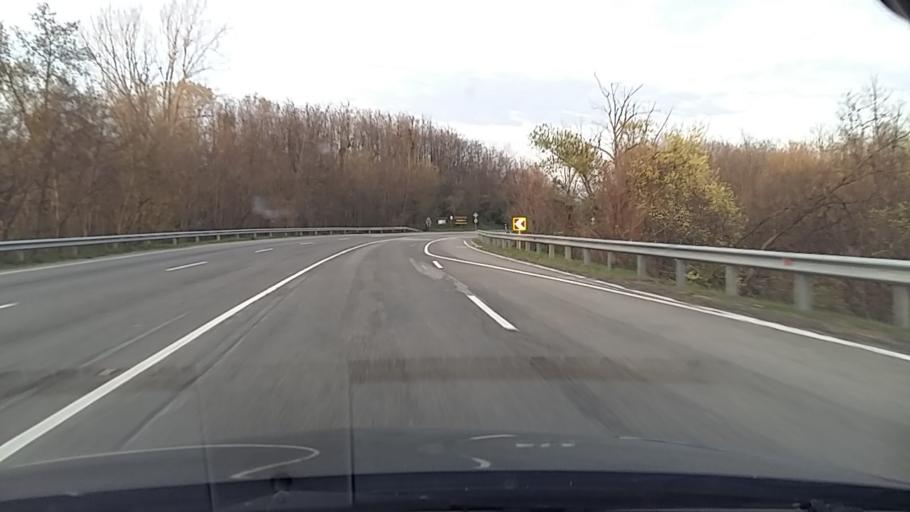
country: HU
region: Baranya
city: Mecseknadasd
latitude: 46.2114
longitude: 18.4578
